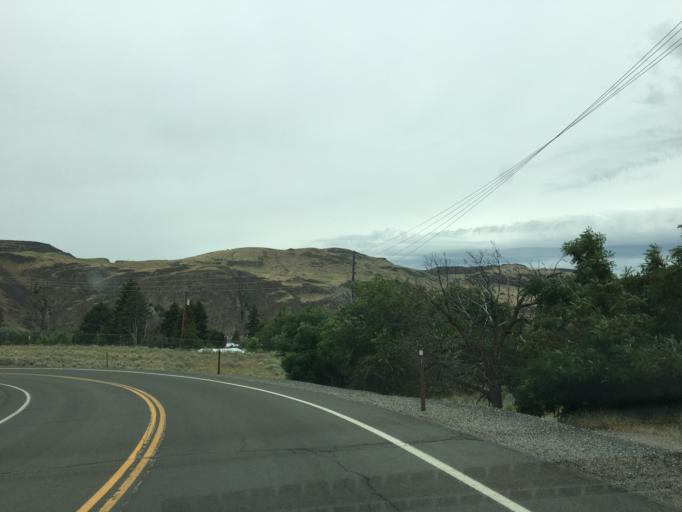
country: US
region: Washington
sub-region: Okanogan County
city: Coulee Dam
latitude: 47.9671
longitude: -118.9700
